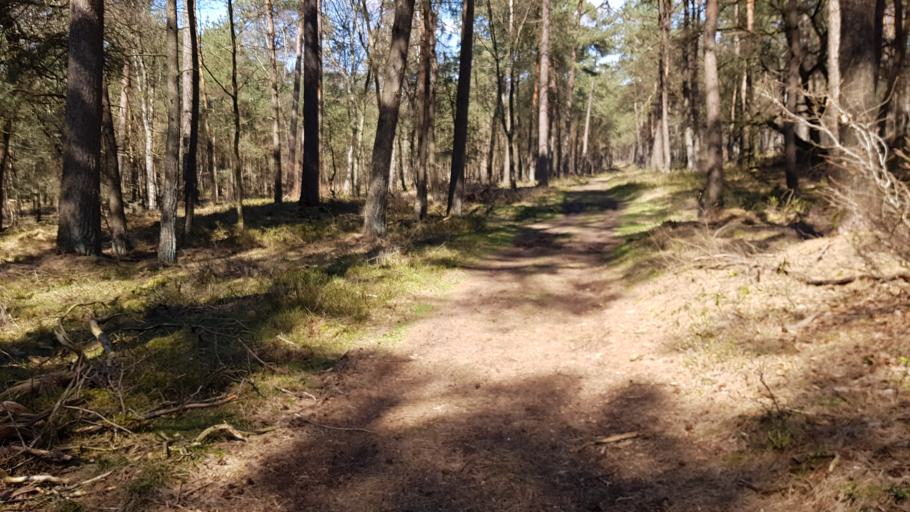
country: NL
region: Gelderland
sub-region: Gemeente Apeldoorn
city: Loenen
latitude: 52.0676
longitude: 6.0069
